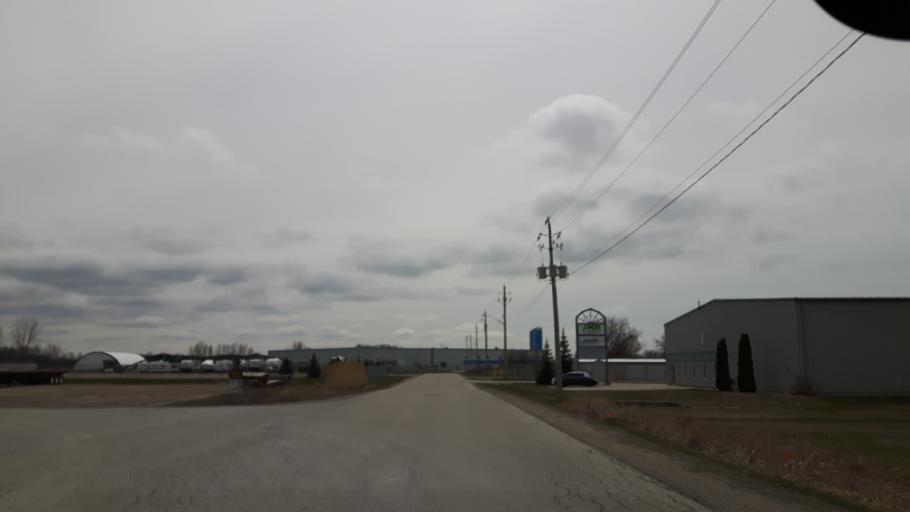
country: CA
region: Ontario
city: Goderich
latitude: 43.7250
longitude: -81.7030
